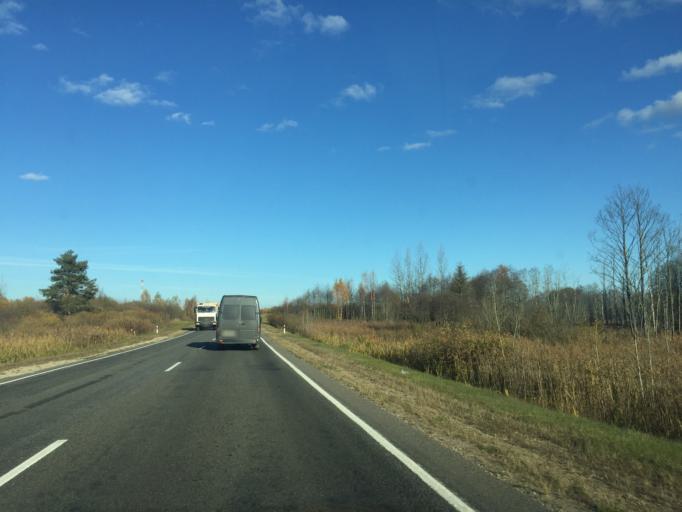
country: BY
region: Vitebsk
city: Dzisna
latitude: 55.2881
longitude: 28.1866
